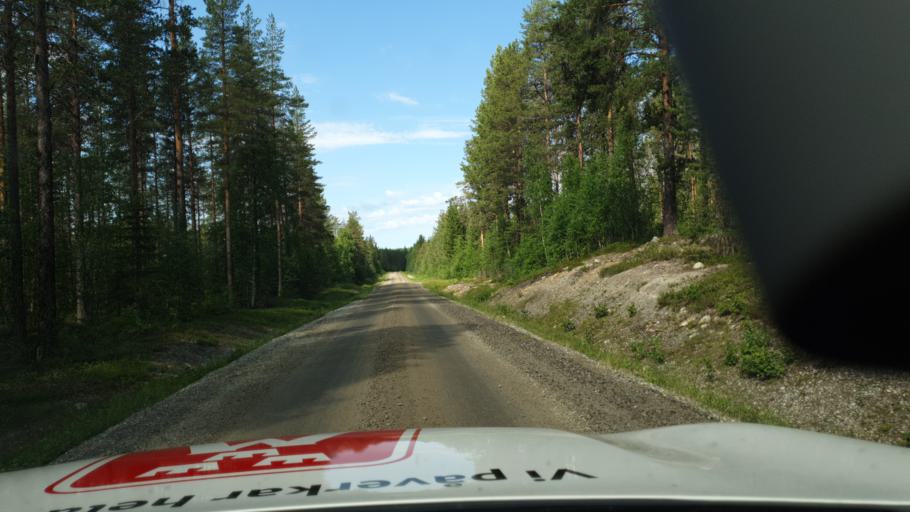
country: SE
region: Vaesterbotten
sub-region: Norsjo Kommun
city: Norsjoe
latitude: 64.6996
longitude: 19.4787
